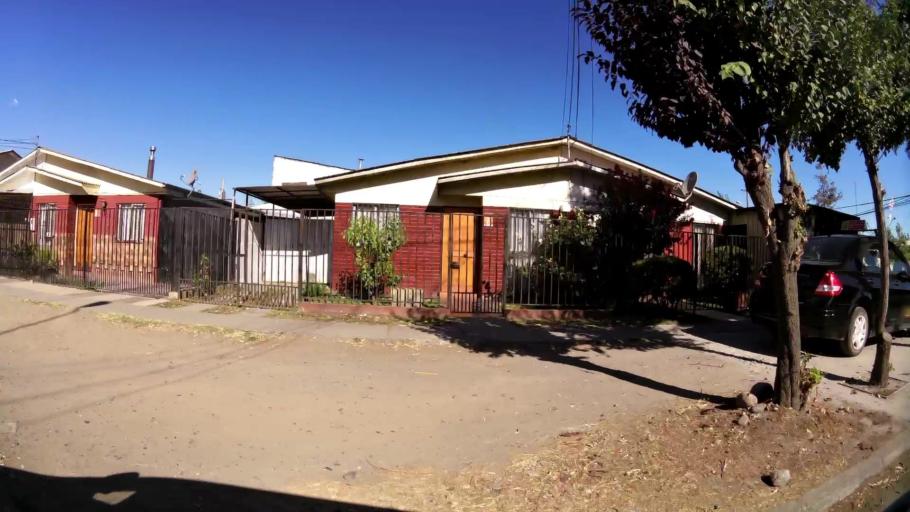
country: CL
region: O'Higgins
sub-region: Provincia de Colchagua
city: Chimbarongo
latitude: -34.5753
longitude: -70.9984
